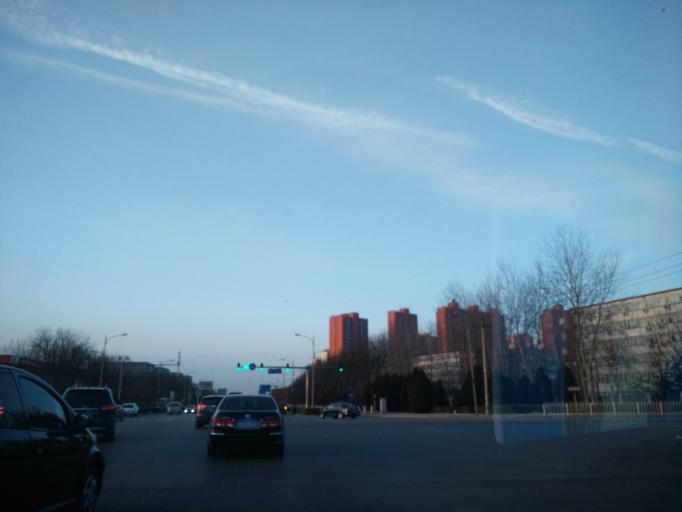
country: CN
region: Beijing
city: Jiugong
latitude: 39.7660
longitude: 116.5083
